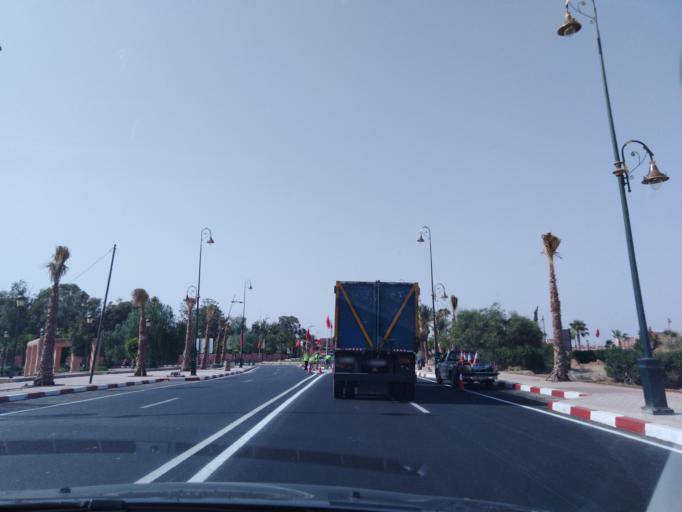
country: MA
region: Marrakech-Tensift-Al Haouz
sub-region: Kelaa-Des-Sraghna
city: Sidi Bou Othmane
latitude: 32.2283
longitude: -7.9570
